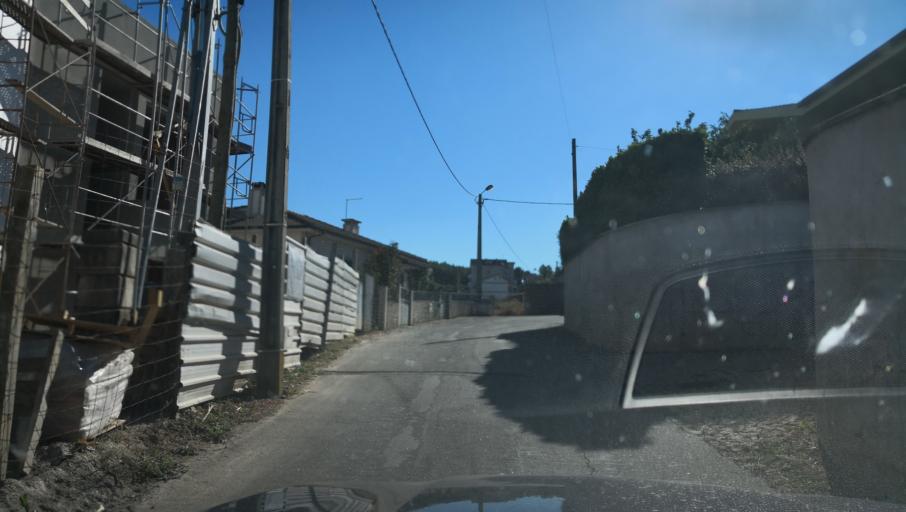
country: PT
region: Vila Real
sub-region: Vila Real
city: Vila Real
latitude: 41.2841
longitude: -7.7215
